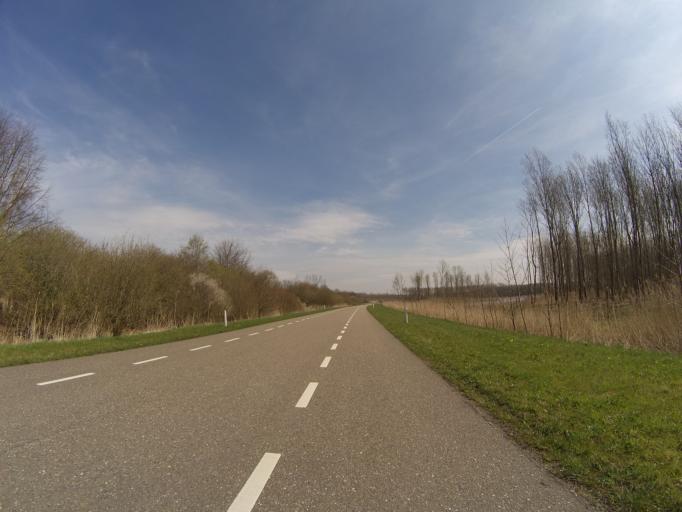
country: NL
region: Flevoland
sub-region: Gemeente Zeewolde
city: Zeewolde
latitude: 52.3132
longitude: 5.4488
